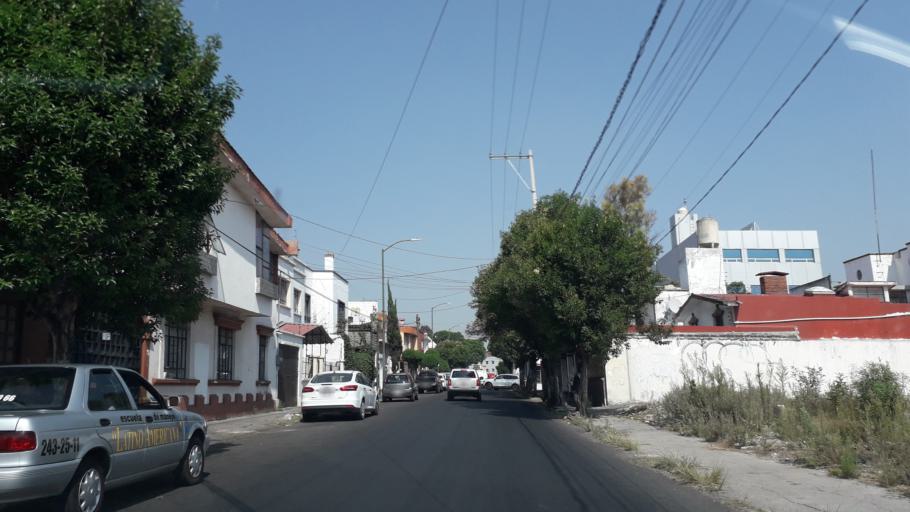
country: MX
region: Puebla
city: Puebla
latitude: 19.0343
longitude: -98.2126
